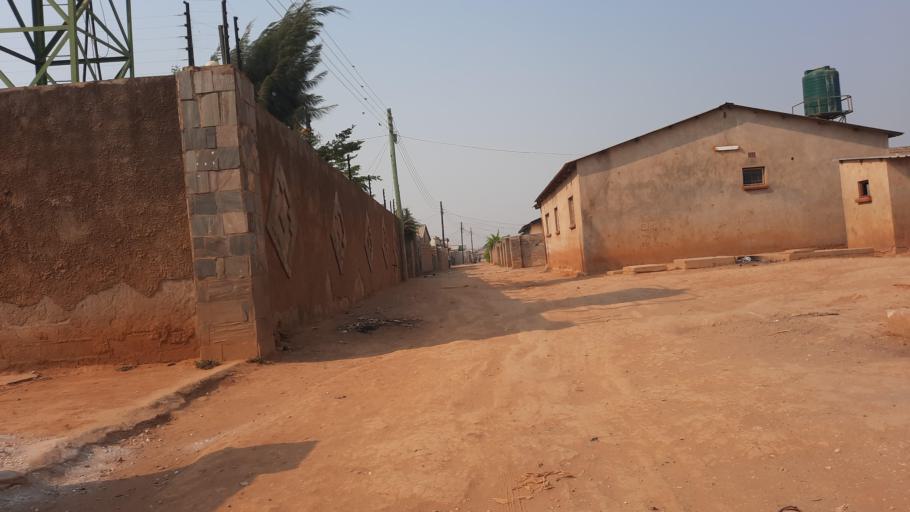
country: ZM
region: Lusaka
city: Lusaka
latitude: -15.3952
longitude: 28.3829
